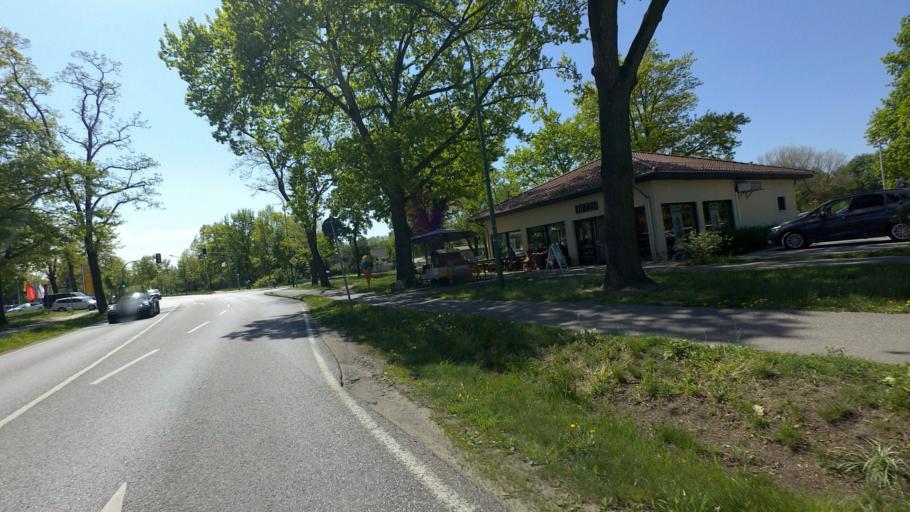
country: DE
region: Brandenburg
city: Konigs Wusterhausen
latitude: 52.2729
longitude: 13.6324
